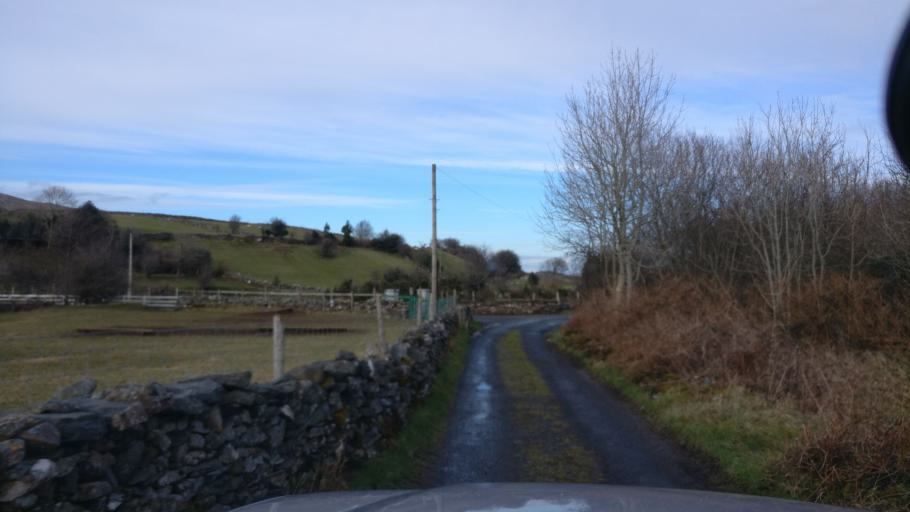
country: IE
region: Connaught
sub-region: County Galway
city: Oughterard
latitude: 53.5536
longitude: -9.4470
